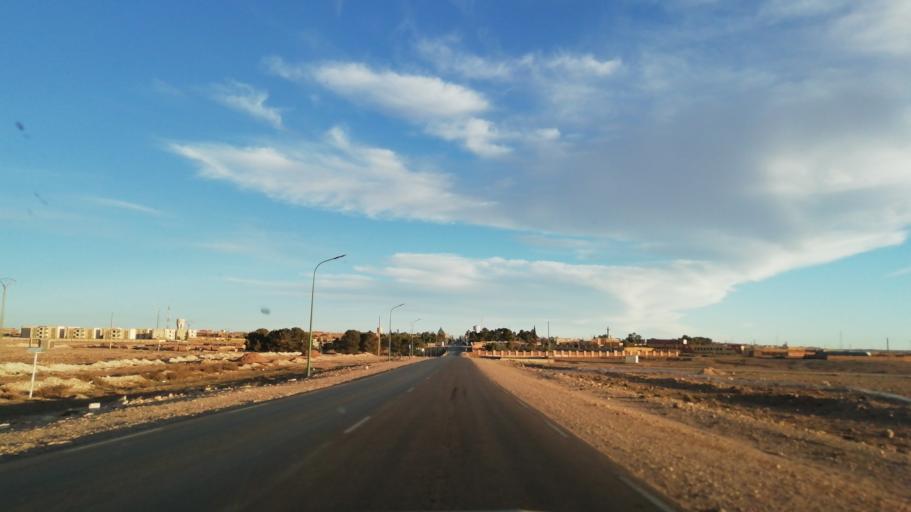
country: DZ
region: Wilaya de Naama
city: Naama
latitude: 33.7222
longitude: -0.7367
